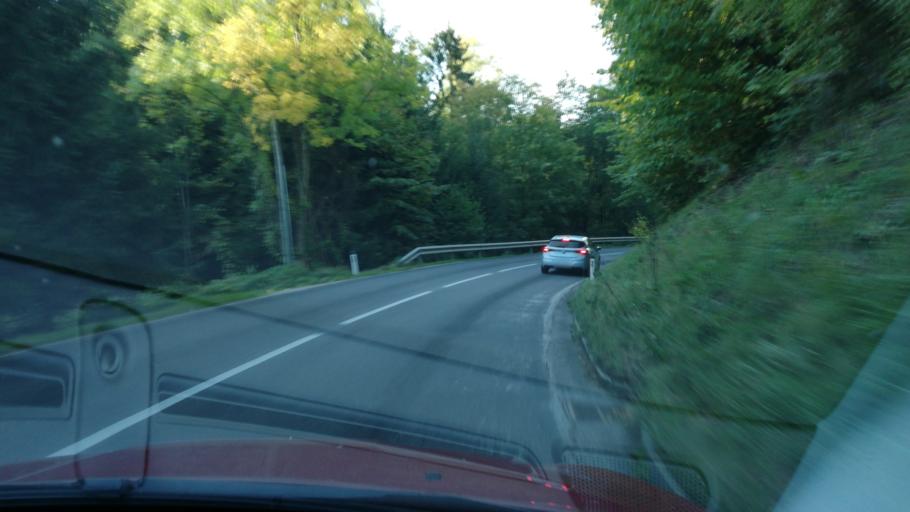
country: AT
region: Upper Austria
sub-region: Politischer Bezirk Kirchdorf an der Krems
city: Gruenburg
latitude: 47.9721
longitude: 14.2704
